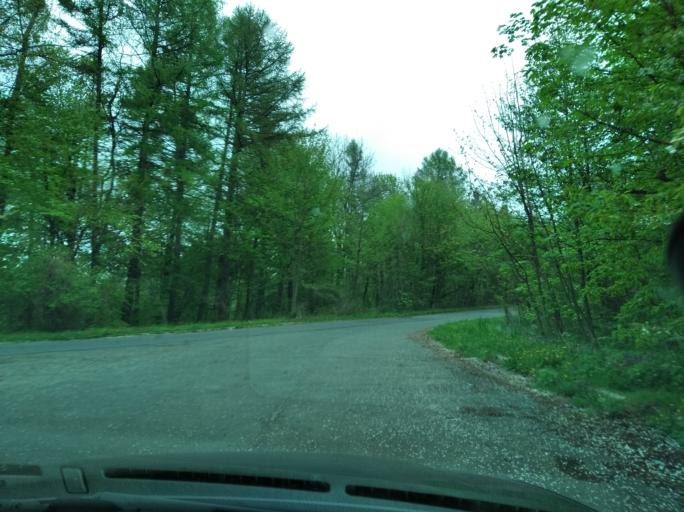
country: PL
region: Subcarpathian Voivodeship
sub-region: Powiat sanocki
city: Tyrawa Woloska
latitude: 49.5543
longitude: 22.3233
